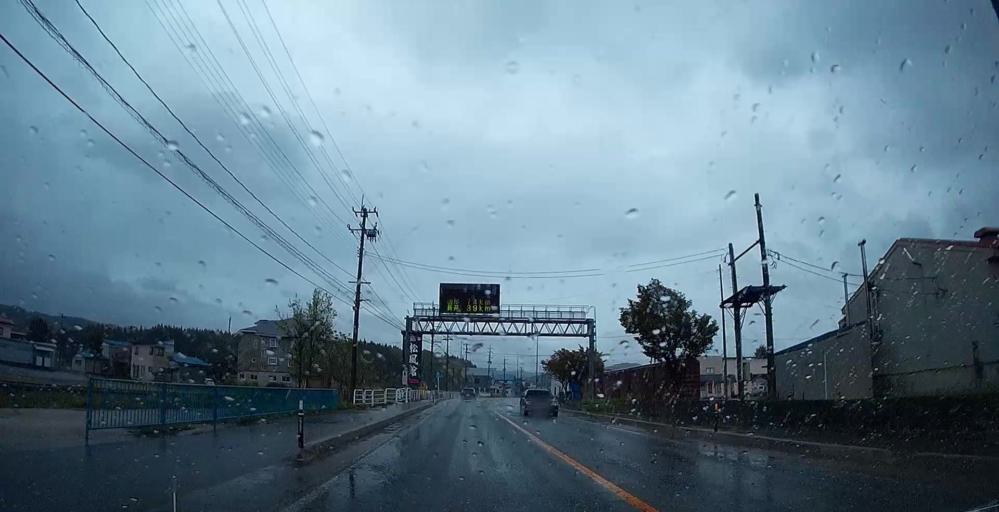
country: JP
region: Yamagata
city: Nagai
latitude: 38.0534
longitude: 139.7564
